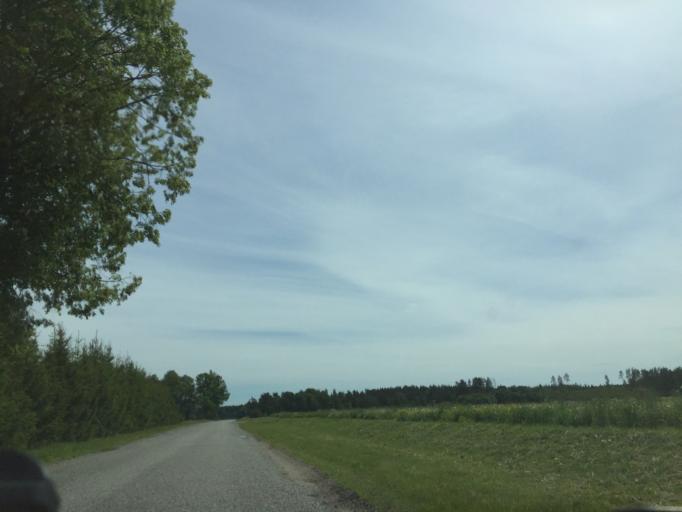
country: LV
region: Koceni
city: Koceni
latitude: 57.5046
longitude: 25.3536
